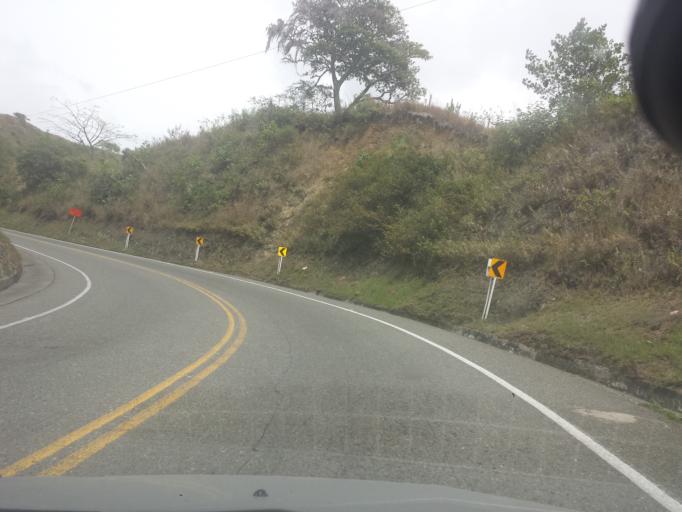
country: CO
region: Antioquia
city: Antioquia
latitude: 6.6085
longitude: -75.8555
